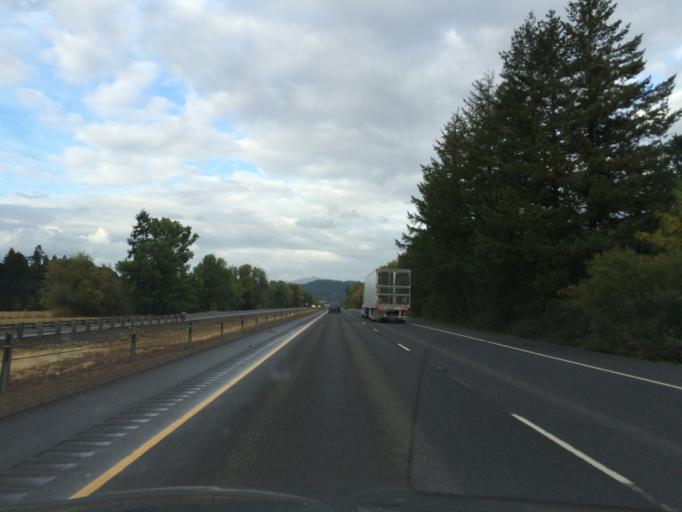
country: US
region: Oregon
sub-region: Lane County
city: Cottage Grove
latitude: 43.7525
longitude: -123.1062
